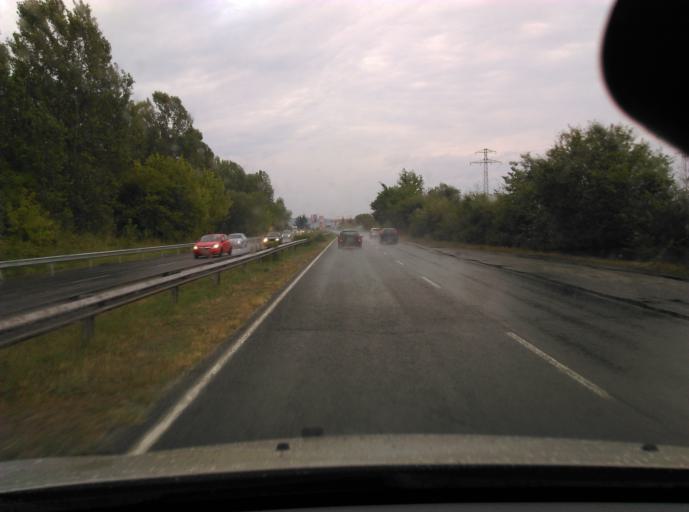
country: BG
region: Burgas
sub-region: Obshtina Burgas
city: Burgas
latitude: 42.4589
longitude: 27.4399
